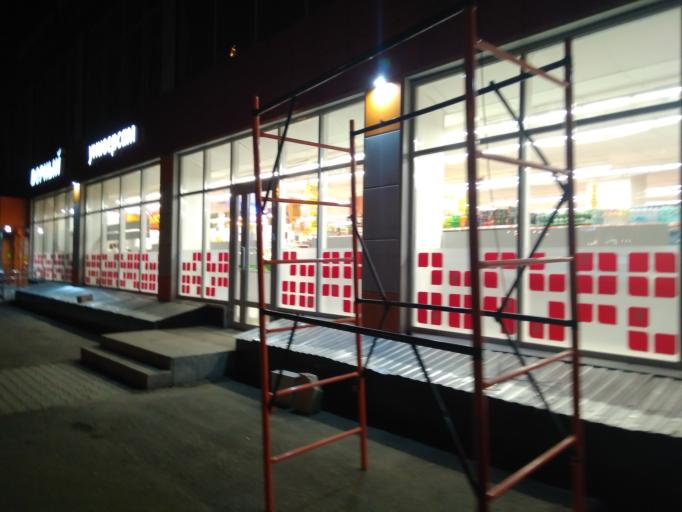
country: RU
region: Moskovskaya
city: Bykovo
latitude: 55.6075
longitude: 38.0961
